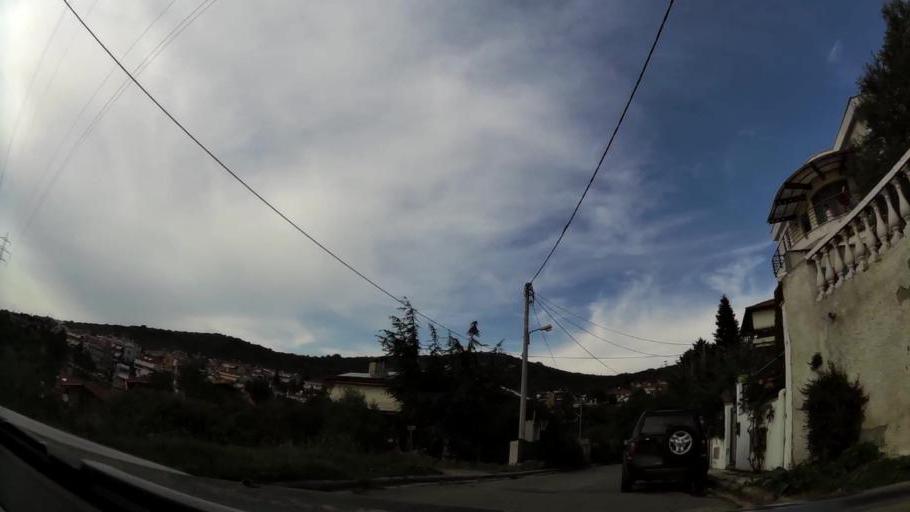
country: GR
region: Central Macedonia
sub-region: Nomos Thessalonikis
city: Pefka
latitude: 40.6595
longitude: 23.0033
